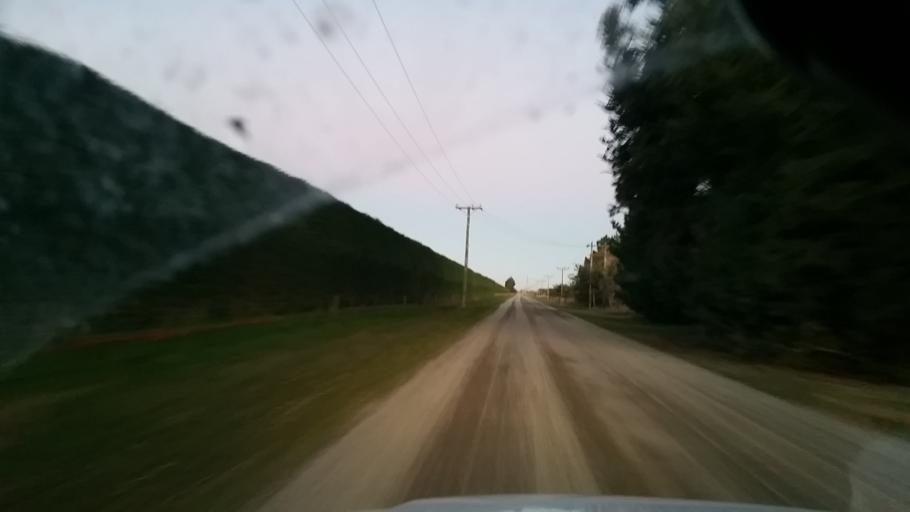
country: NZ
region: Canterbury
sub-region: Ashburton District
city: Tinwald
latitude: -43.9701
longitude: 171.6362
